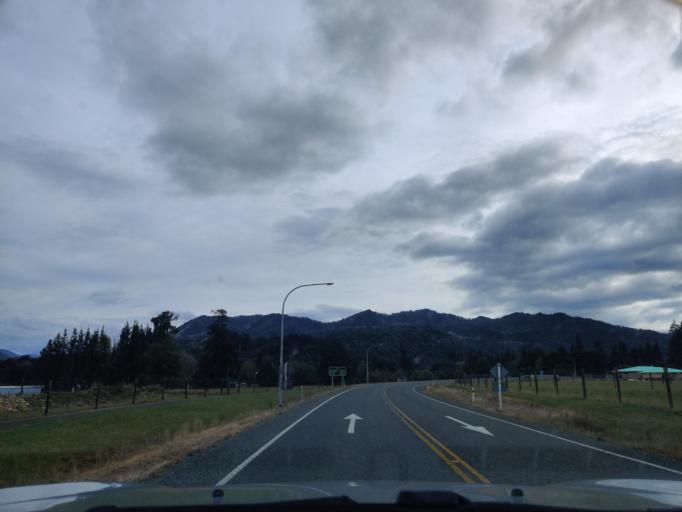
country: NZ
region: West Coast
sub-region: Buller District
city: Westport
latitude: -41.7984
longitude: 172.3375
